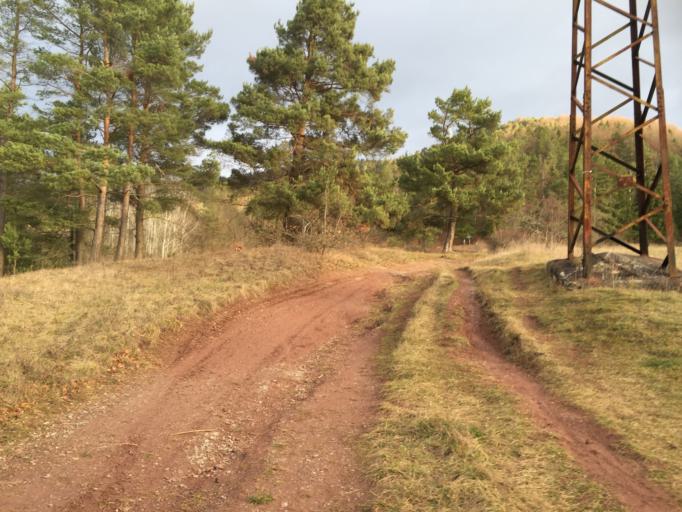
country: DE
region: Thuringia
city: Bad Blankenburg
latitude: 50.6928
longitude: 11.2622
